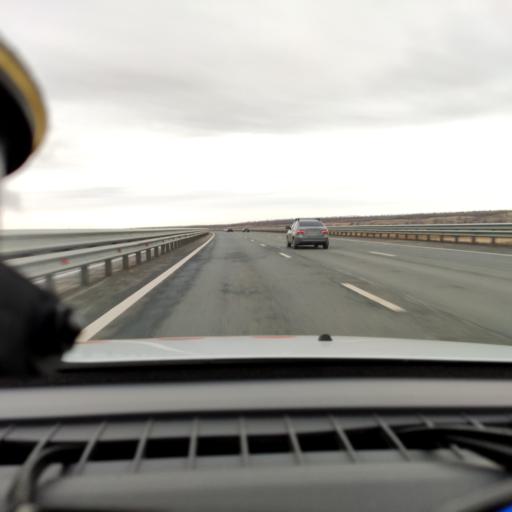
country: RU
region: Samara
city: Smyshlyayevka
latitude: 53.1600
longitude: 50.3295
